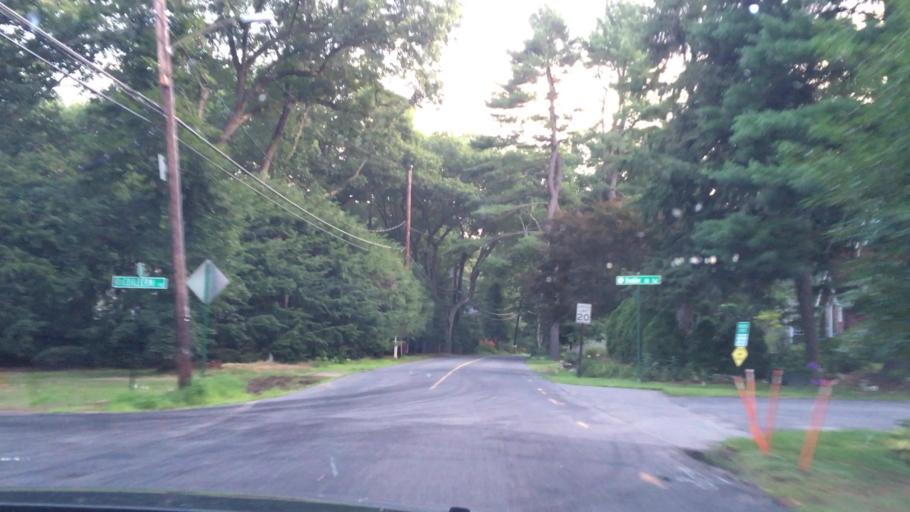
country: US
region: Massachusetts
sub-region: Norfolk County
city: Wellesley
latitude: 42.3269
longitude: -71.2742
